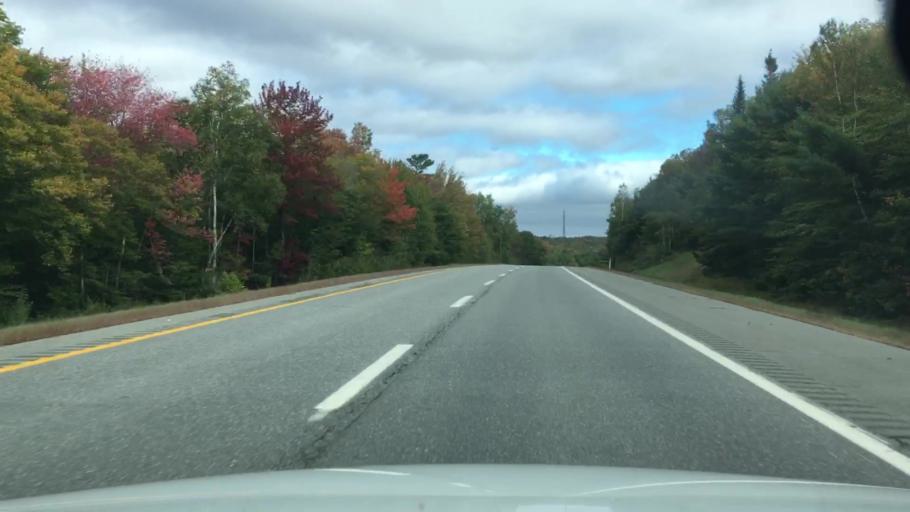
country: US
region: Maine
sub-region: Penobscot County
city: Carmel
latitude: 44.7725
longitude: -69.0096
